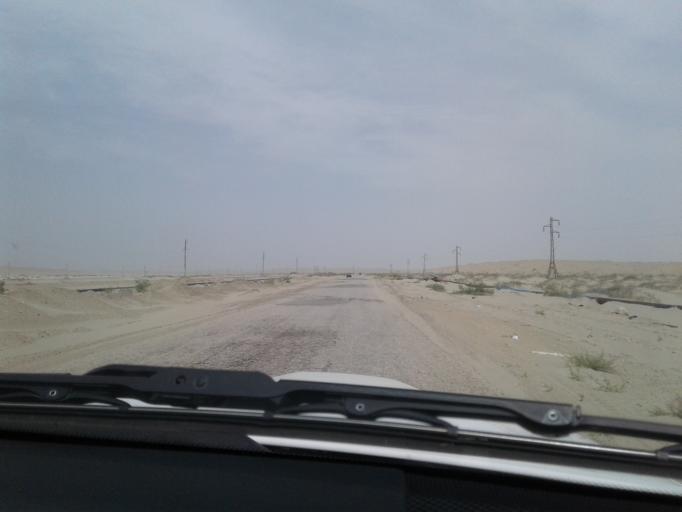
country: TM
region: Balkan
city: Turkmenbasy
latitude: 39.3897
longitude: 53.5028
